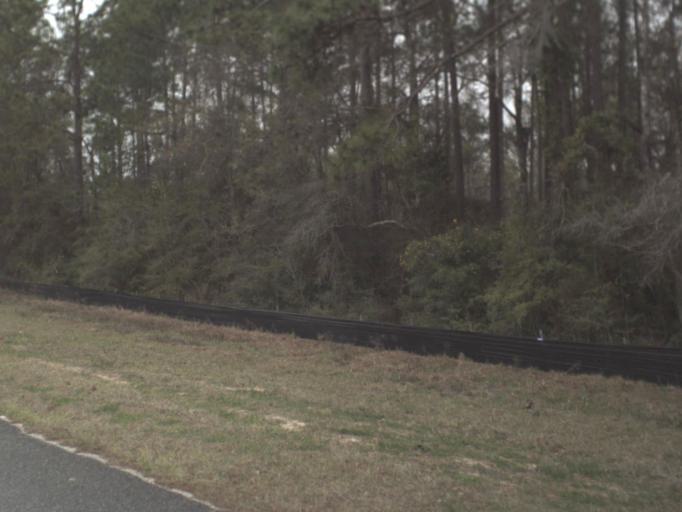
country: US
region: Florida
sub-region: Wakulla County
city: Crawfordville
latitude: 30.1391
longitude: -84.3208
